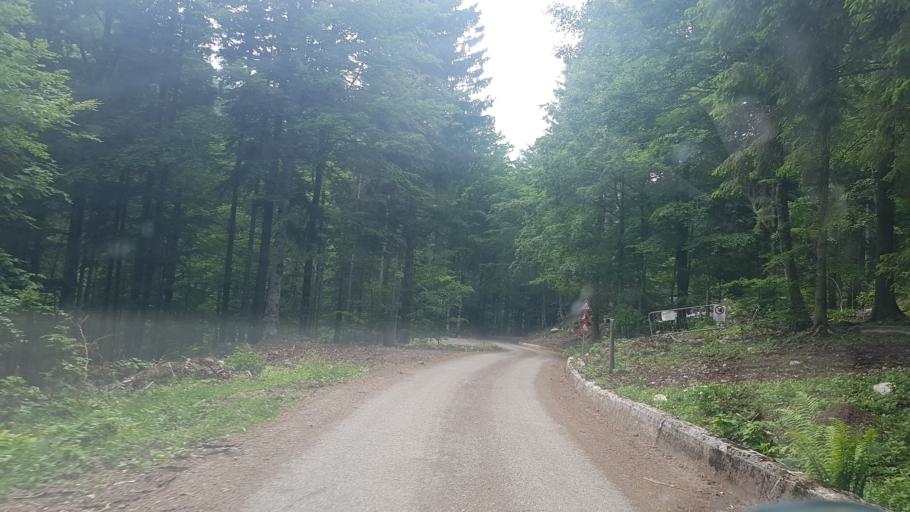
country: IT
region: Friuli Venezia Giulia
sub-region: Provincia di Udine
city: Paularo
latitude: 46.5365
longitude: 13.2070
